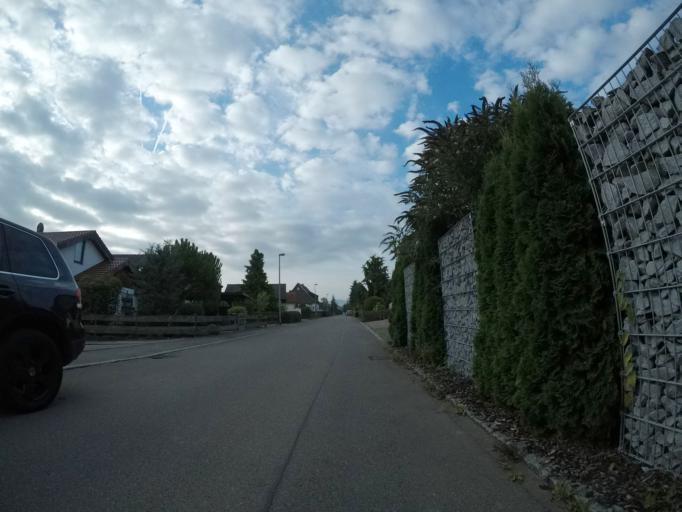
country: DE
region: Baden-Wuerttemberg
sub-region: Tuebingen Region
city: Sickenhausen
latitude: 48.5207
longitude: 9.1735
